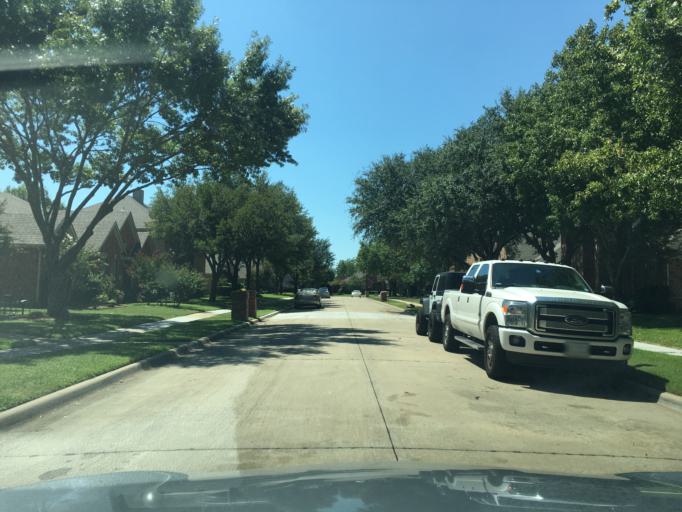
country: US
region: Texas
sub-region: Dallas County
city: Sachse
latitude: 32.9667
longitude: -96.6336
